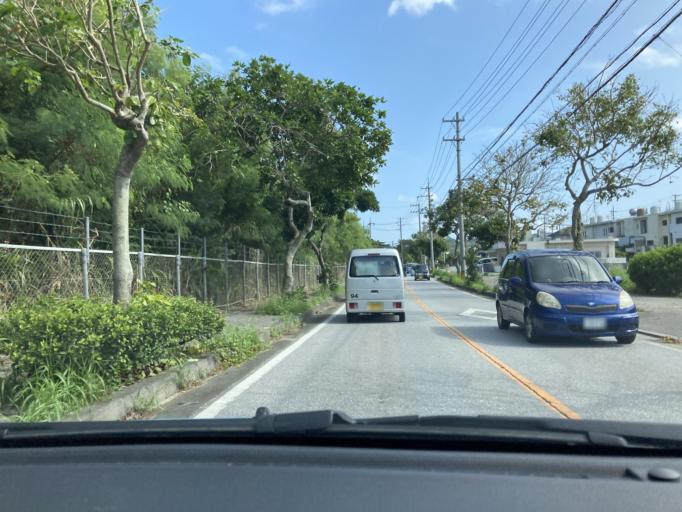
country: JP
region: Okinawa
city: Ginowan
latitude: 26.2781
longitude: 127.7833
